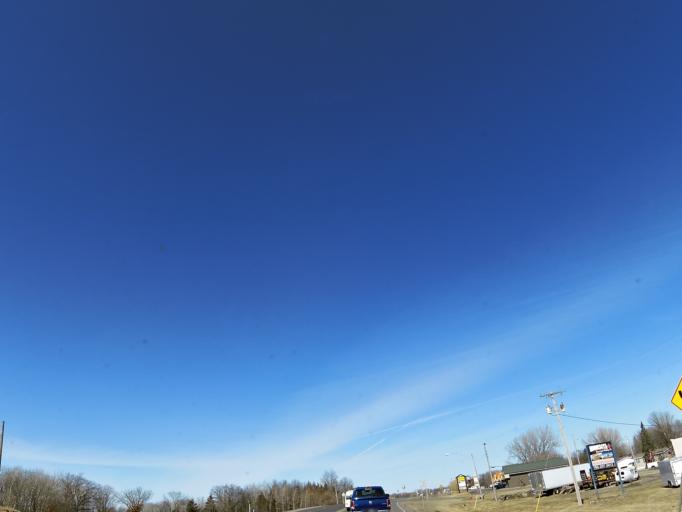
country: US
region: Minnesota
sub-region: Wright County
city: Rockford
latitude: 45.0808
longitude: -93.7275
